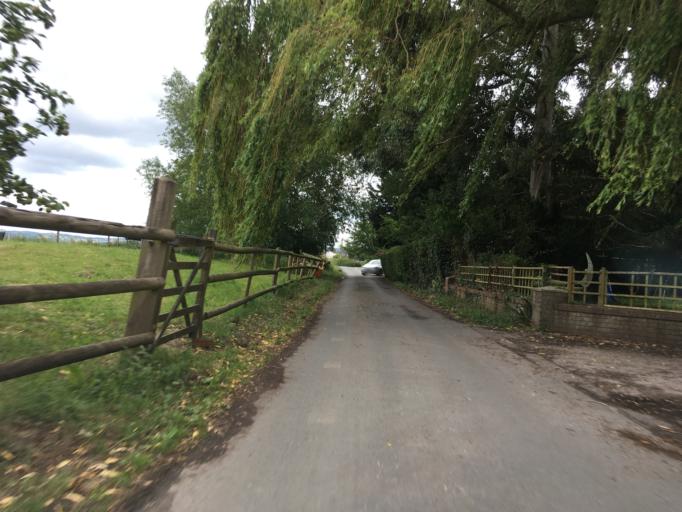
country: GB
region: England
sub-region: Gloucestershire
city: Stonehouse
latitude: 51.7929
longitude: -2.3760
